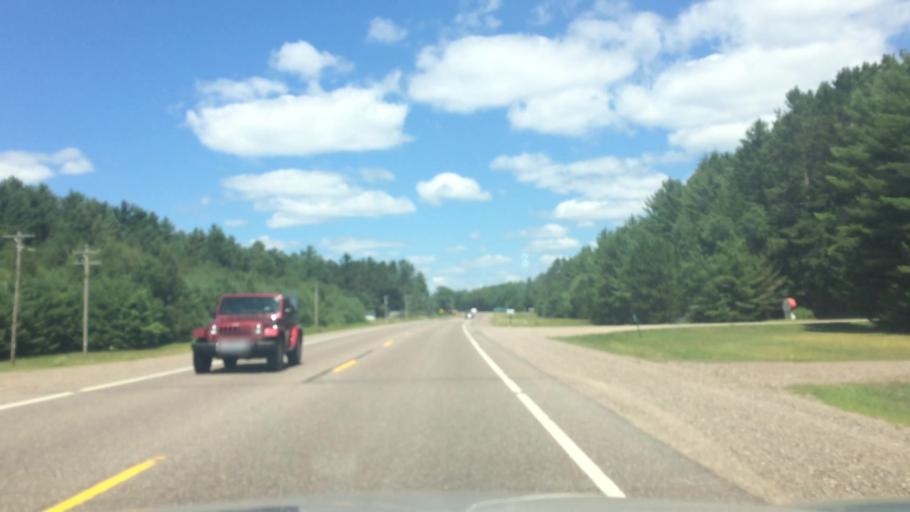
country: US
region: Wisconsin
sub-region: Vilas County
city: Lac du Flambeau
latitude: 45.9359
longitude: -89.6966
